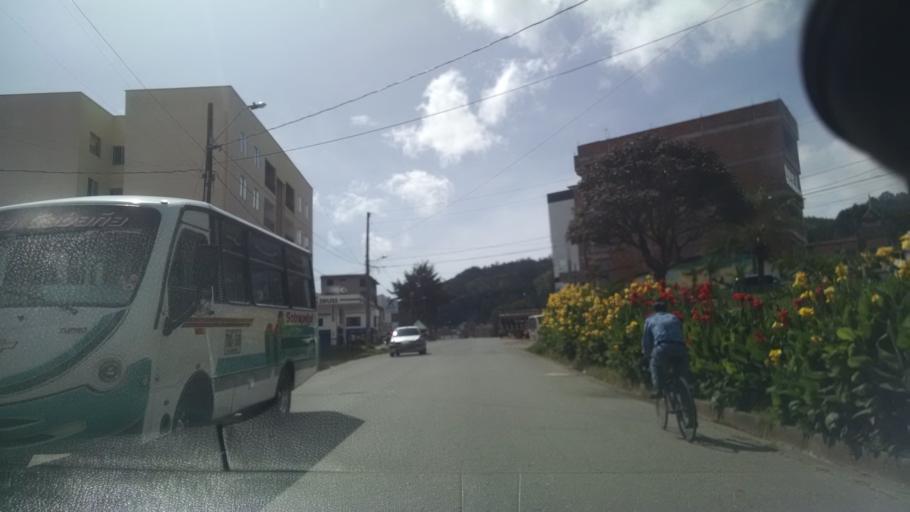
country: CO
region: Antioquia
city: Guatape
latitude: 6.2220
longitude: -75.2464
